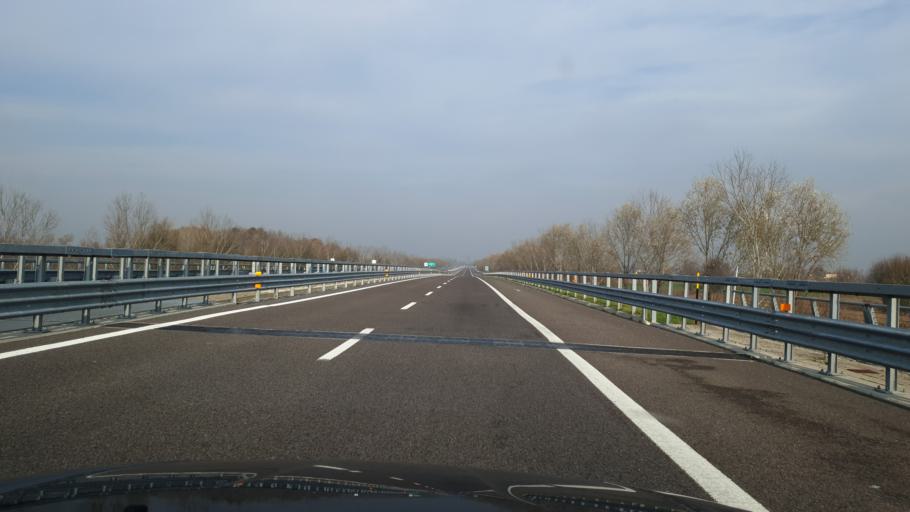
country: IT
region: Veneto
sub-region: Provincia di Padova
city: Megliadino San Vitale
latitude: 45.1621
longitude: 11.5340
